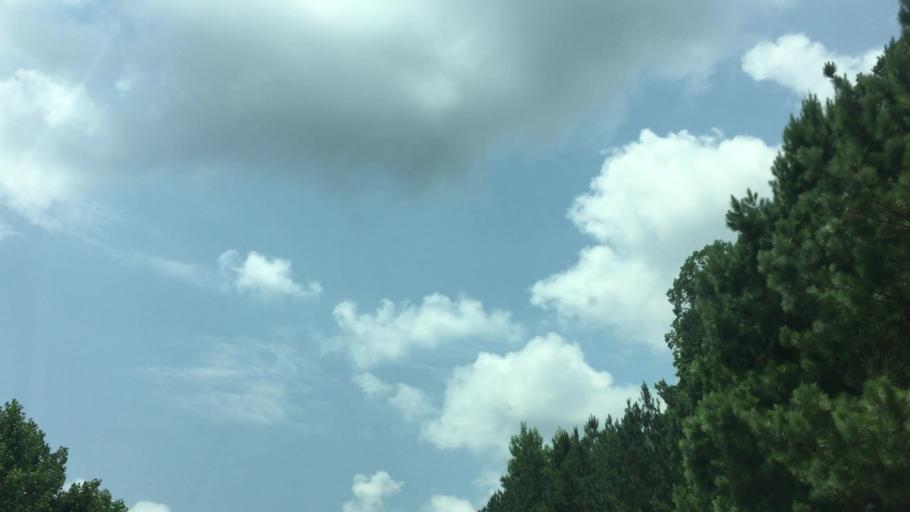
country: US
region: Georgia
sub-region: Fulton County
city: Chattahoochee Hills
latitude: 33.5685
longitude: -84.7343
